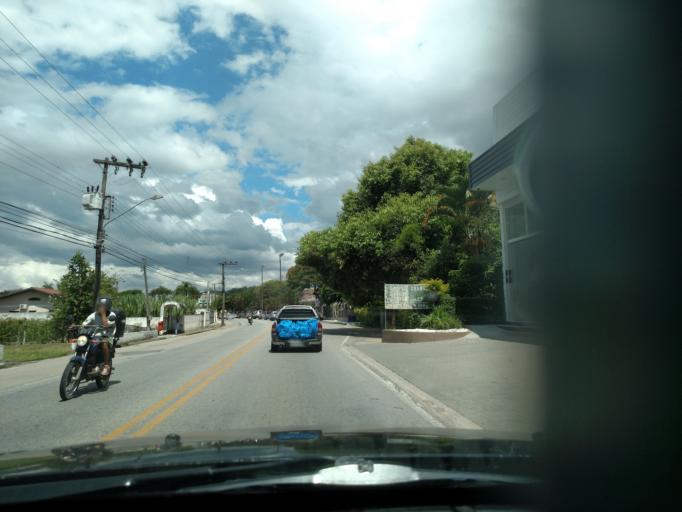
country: BR
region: Santa Catarina
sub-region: Gaspar
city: Gaspar
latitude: -26.9251
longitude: -48.9674
